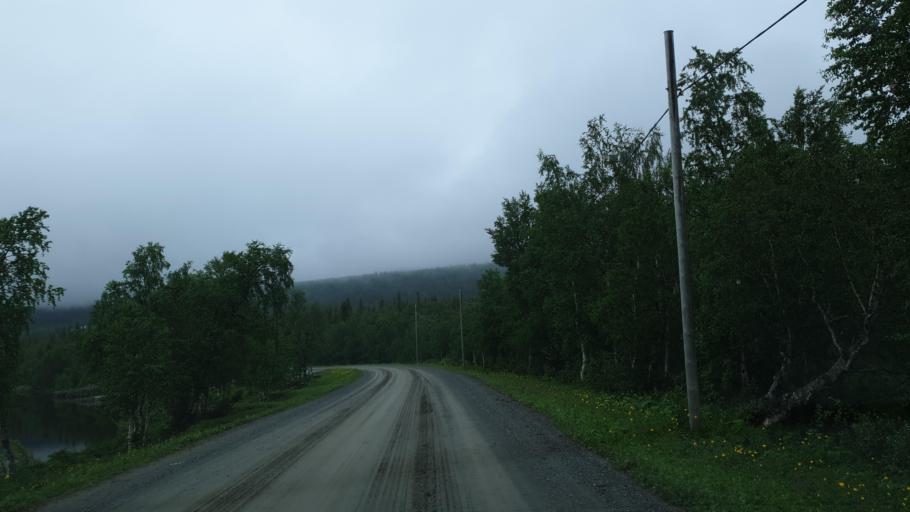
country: SE
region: Vaesterbotten
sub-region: Vilhelmina Kommun
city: Sjoberg
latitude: 65.3359
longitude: 15.8729
